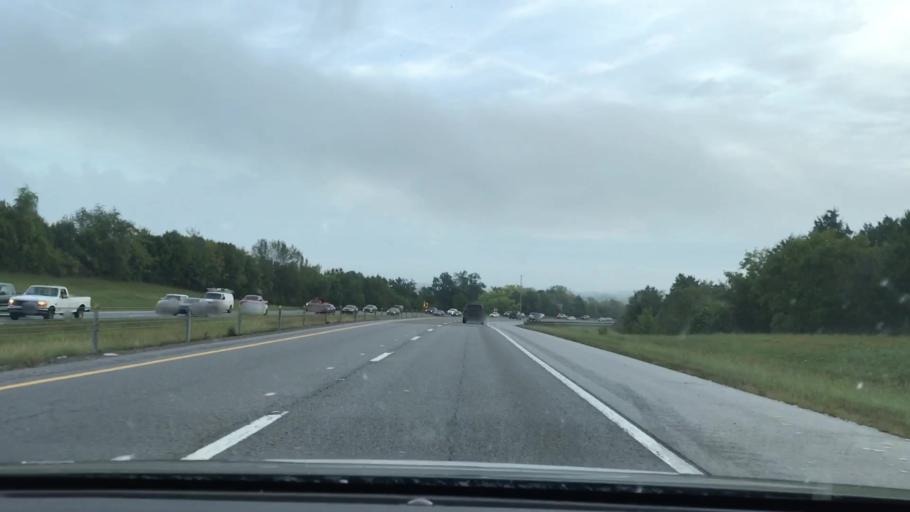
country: US
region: Tennessee
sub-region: Sumner County
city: Hendersonville
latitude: 36.3280
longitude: -86.6310
